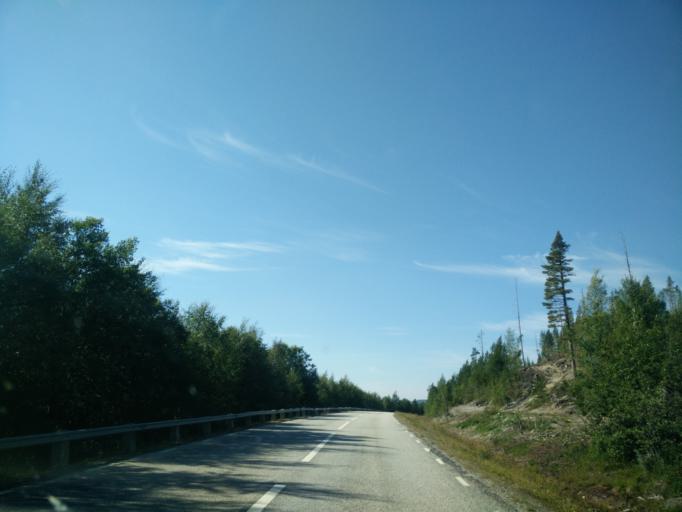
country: SE
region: Jaemtland
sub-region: Are Kommun
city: Jarpen
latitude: 62.8001
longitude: 13.5665
